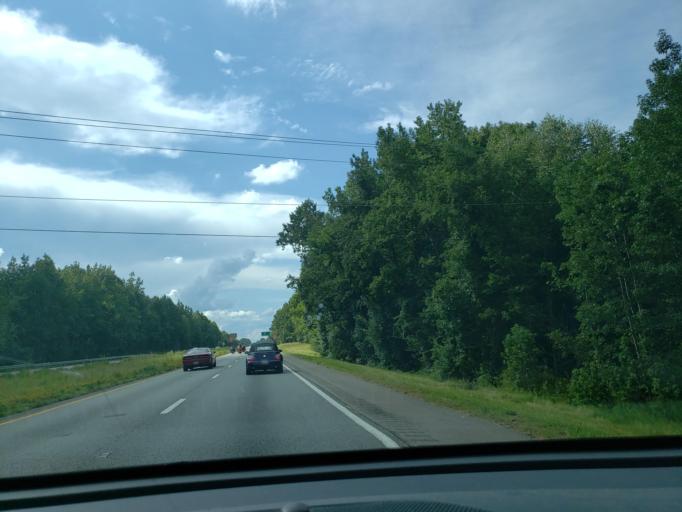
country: US
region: Virginia
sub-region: City of Franklin
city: Franklin
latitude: 36.6487
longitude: -76.9133
